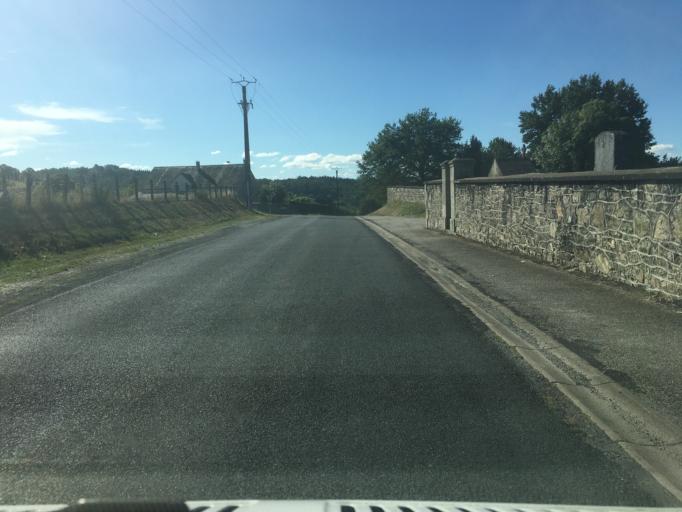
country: FR
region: Auvergne
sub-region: Departement du Cantal
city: Lanobre
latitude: 45.4374
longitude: 2.5290
